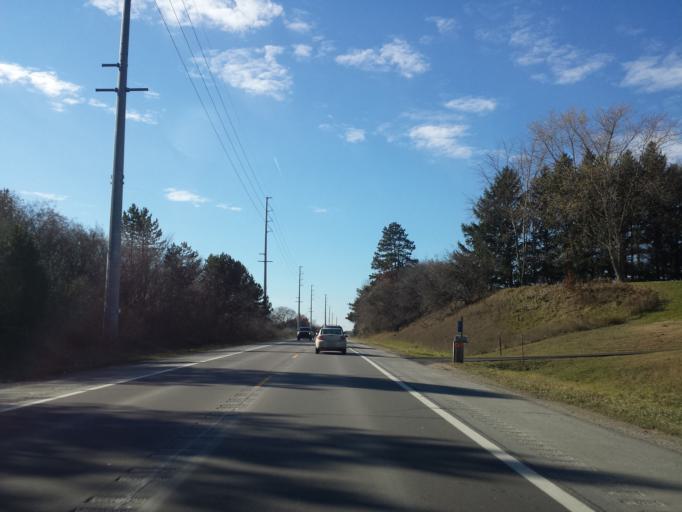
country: US
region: Michigan
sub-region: Livingston County
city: Brighton
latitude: 42.6310
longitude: -83.8033
